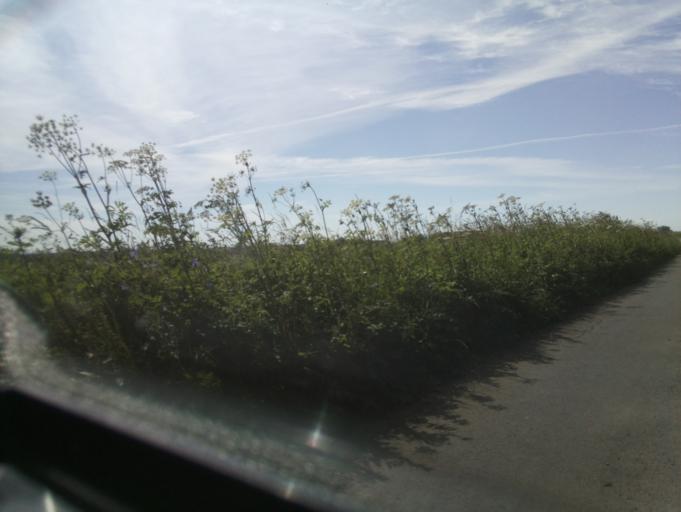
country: GB
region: England
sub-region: Wiltshire
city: Nettleton
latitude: 51.5212
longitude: -2.3080
